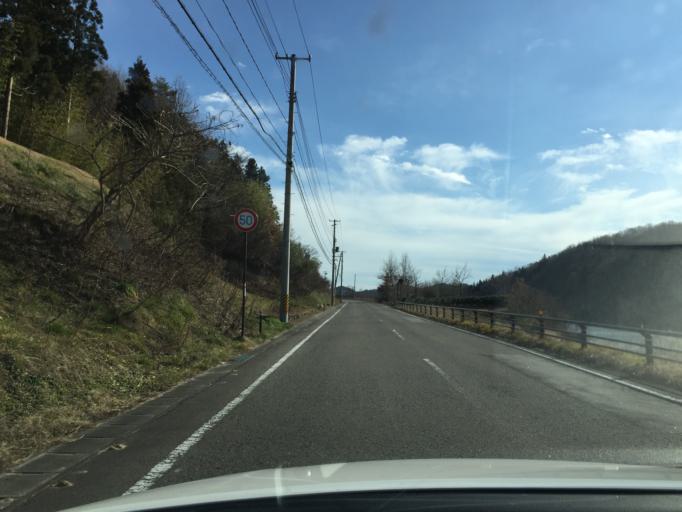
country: JP
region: Fukushima
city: Funehikimachi-funehiki
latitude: 37.2823
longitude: 140.5827
